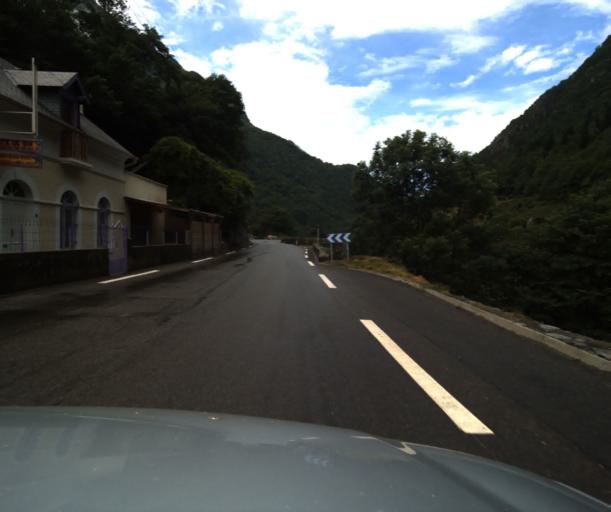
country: FR
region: Midi-Pyrenees
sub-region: Departement des Hautes-Pyrenees
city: Luz-Saint-Sauveur
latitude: 42.8366
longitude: -0.0032
